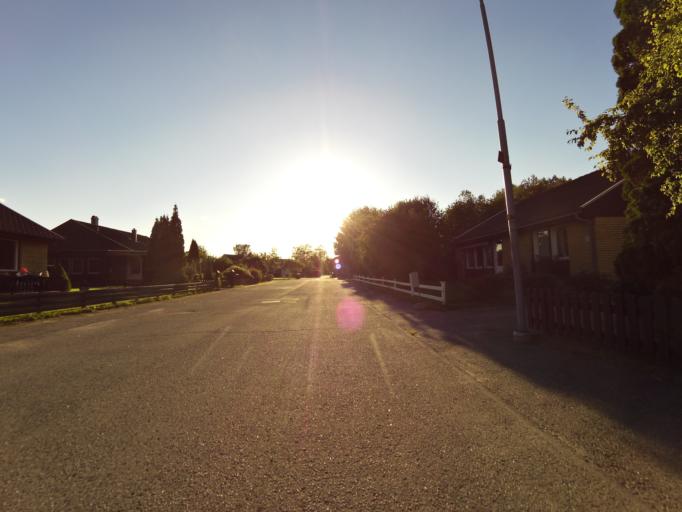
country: SE
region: Gaevleborg
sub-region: Gavle Kommun
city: Gavle
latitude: 60.7155
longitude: 17.1470
